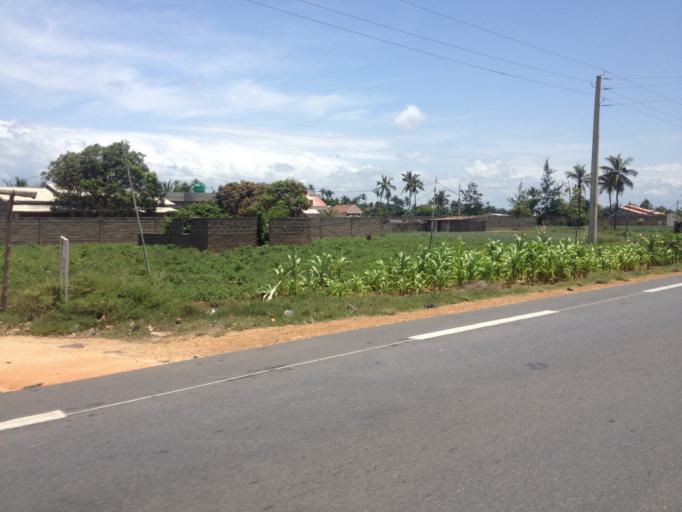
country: BJ
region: Mono
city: Grand-Popo
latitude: 6.2692
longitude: 1.7799
